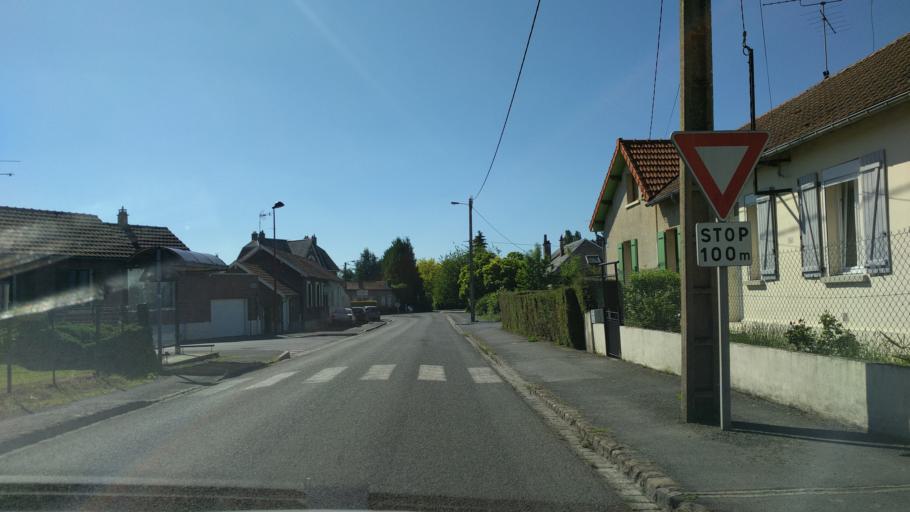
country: FR
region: Picardie
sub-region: Departement de la Somme
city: Peronne
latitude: 49.9360
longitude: 2.9269
